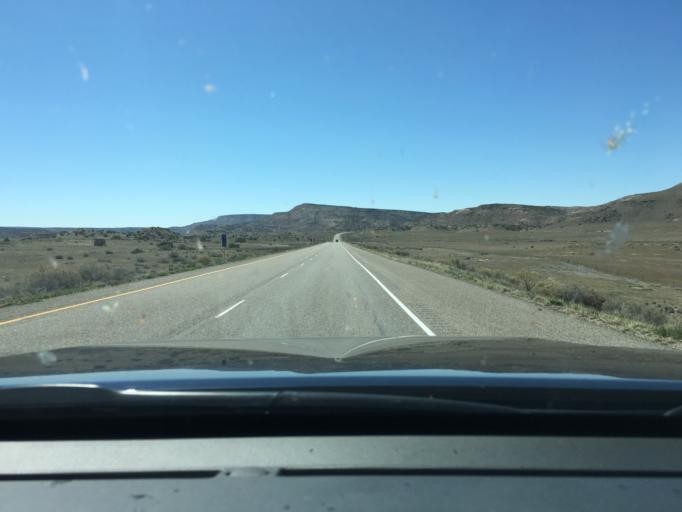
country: US
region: Colorado
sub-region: Mesa County
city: Loma
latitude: 39.2010
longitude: -108.9909
